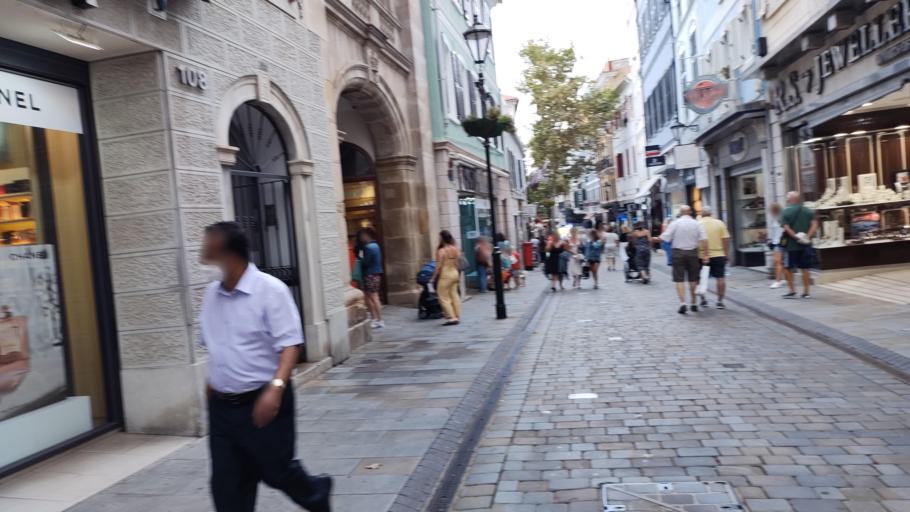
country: GI
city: Gibraltar
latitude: 36.1418
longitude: -5.3533
